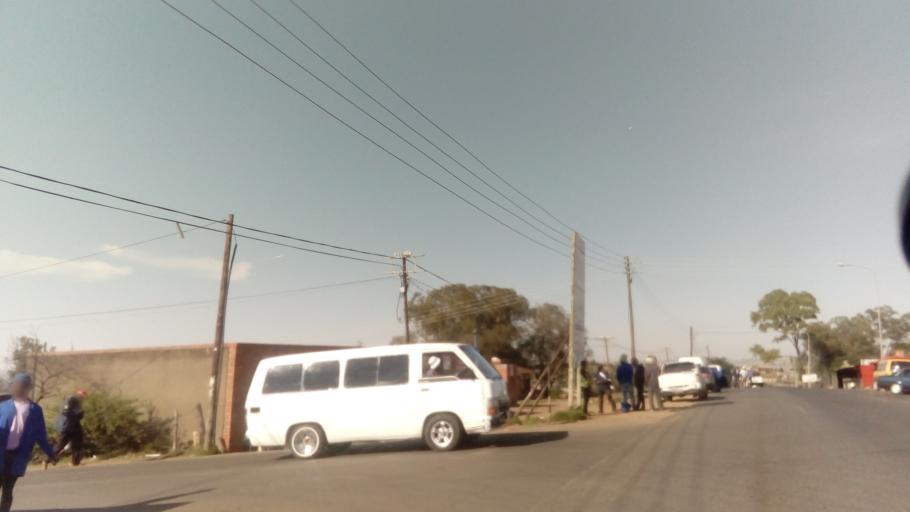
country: LS
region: Berea
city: Teyateyaneng
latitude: -29.1529
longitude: 27.7431
